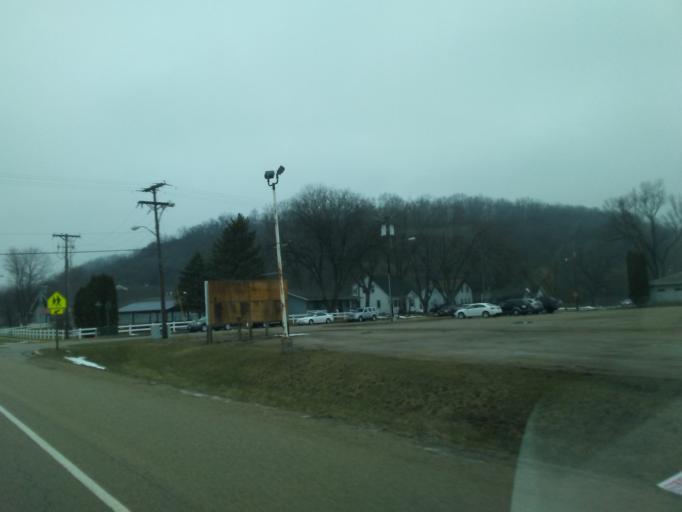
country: US
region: Wisconsin
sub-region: Dane County
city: Black Earth
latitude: 43.1426
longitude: -89.7461
